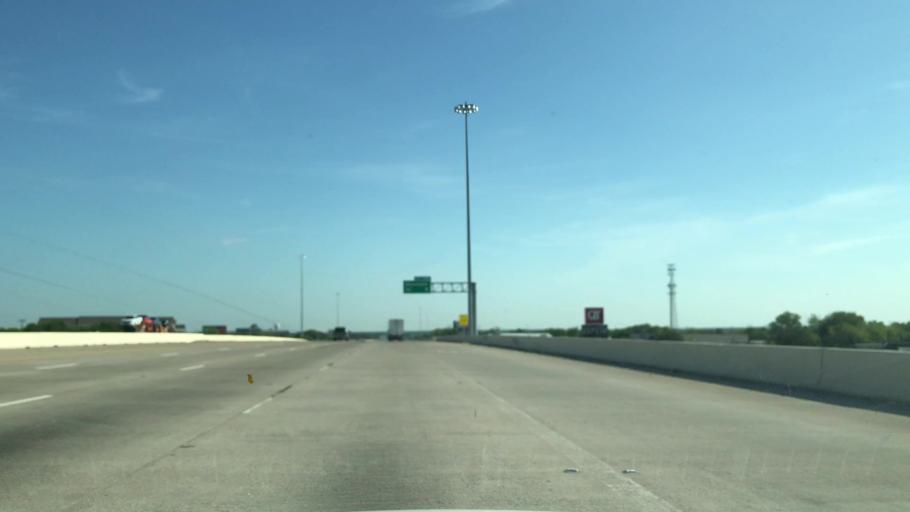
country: US
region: Texas
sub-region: Collin County
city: McKinney
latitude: 33.2289
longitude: -96.6328
